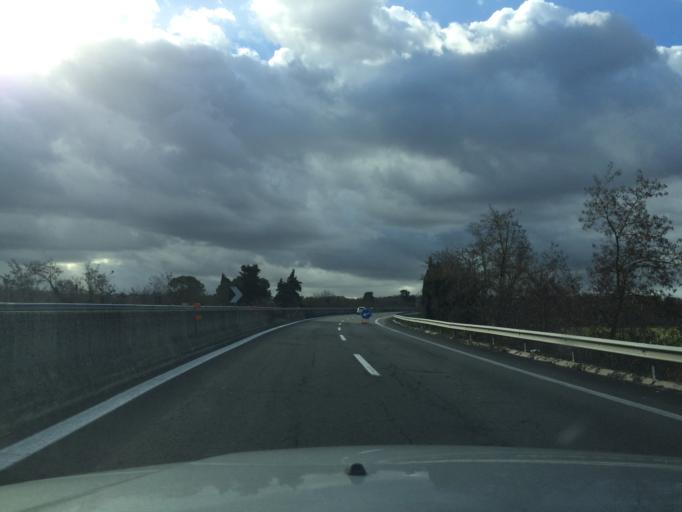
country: IT
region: Umbria
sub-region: Provincia di Terni
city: Acquasparta
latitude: 42.6699
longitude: 12.5529
